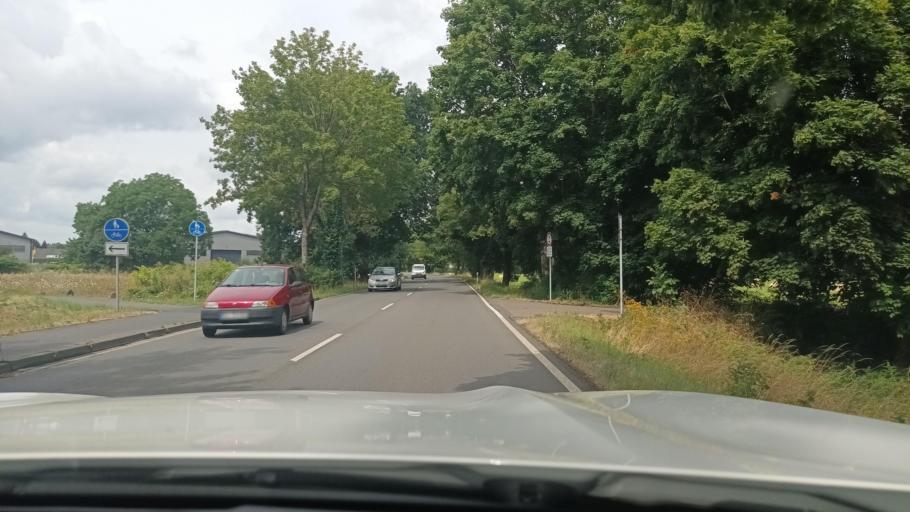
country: DE
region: North Rhine-Westphalia
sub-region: Regierungsbezirk Koln
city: Eitorf
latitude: 50.7727
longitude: 7.4702
